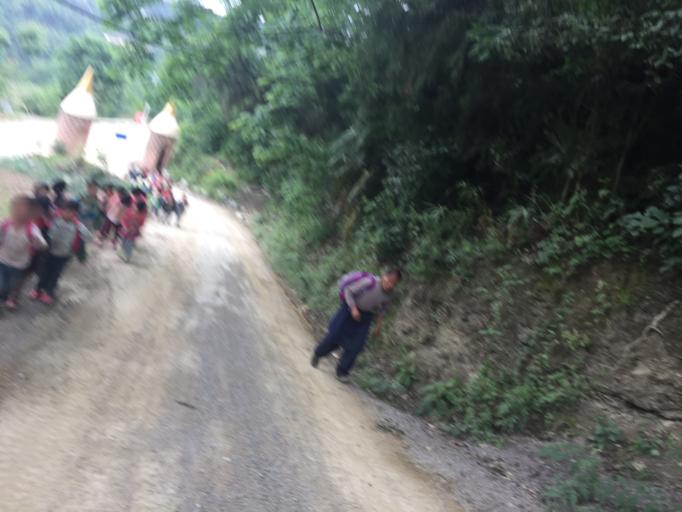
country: CN
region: Guizhou Sheng
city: Xujiaba
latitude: 27.7125
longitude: 108.1292
